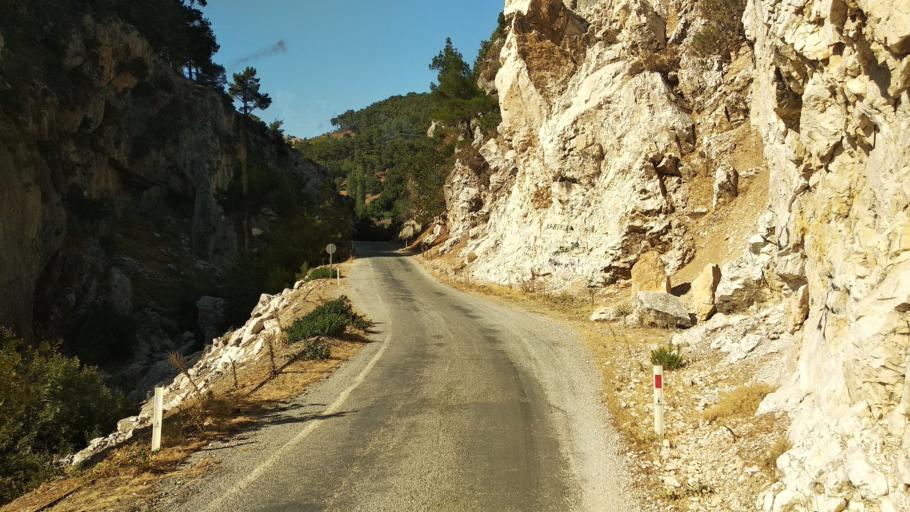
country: TR
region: Izmir
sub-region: Seferihisar
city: Seferhisar
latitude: 38.3215
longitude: 26.9573
